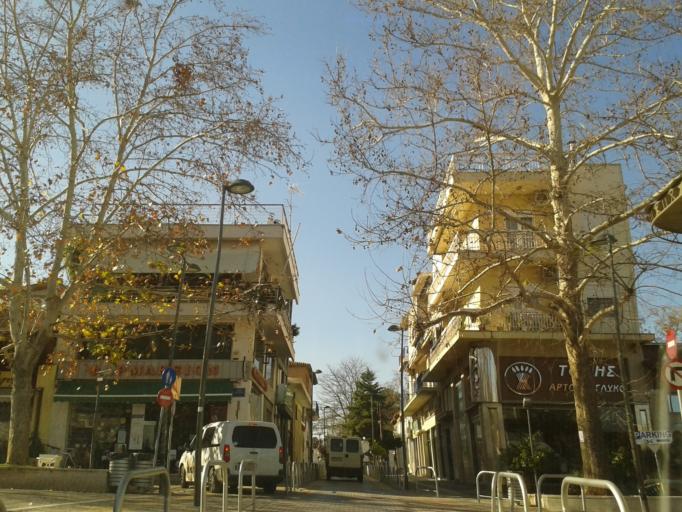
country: GR
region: Central Greece
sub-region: Nomos Voiotias
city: Thivai
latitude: 38.3204
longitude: 23.3173
